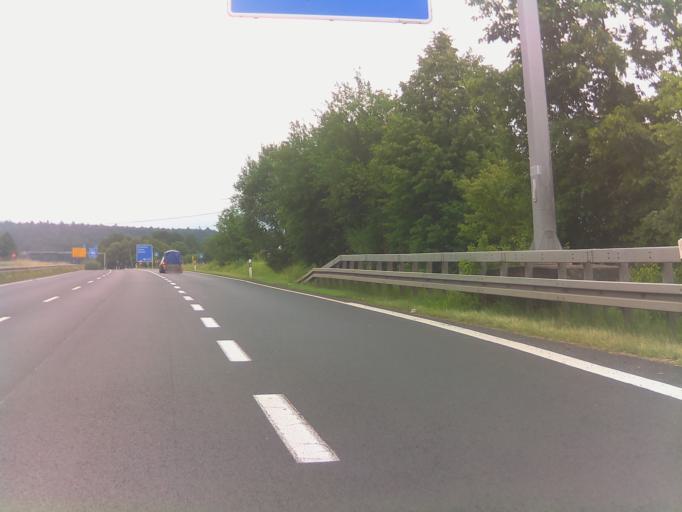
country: DE
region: Hesse
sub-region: Regierungsbezirk Kassel
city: Eichenzell
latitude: 50.4915
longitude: 9.6856
